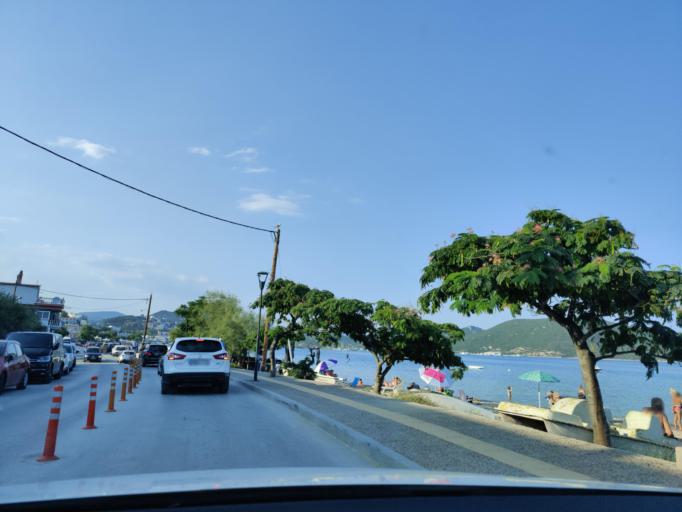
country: GR
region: East Macedonia and Thrace
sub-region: Nomos Kavalas
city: Nea Peramos
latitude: 40.8354
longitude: 24.3053
